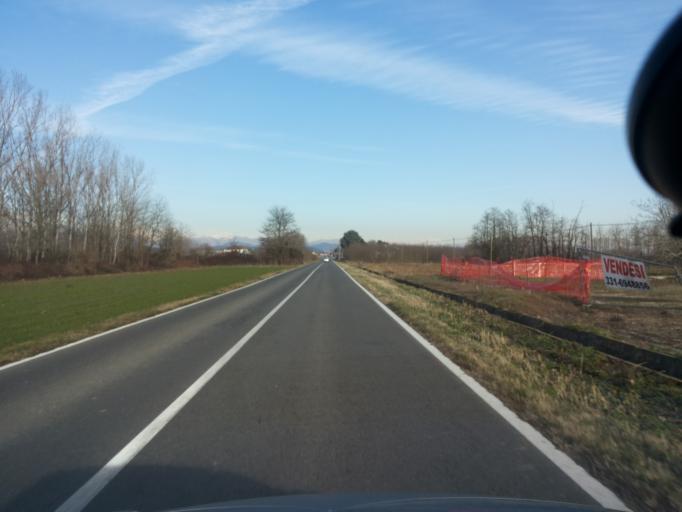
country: IT
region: Piedmont
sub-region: Provincia di Vercelli
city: Ghislarengo
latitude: 45.5175
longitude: 8.3870
